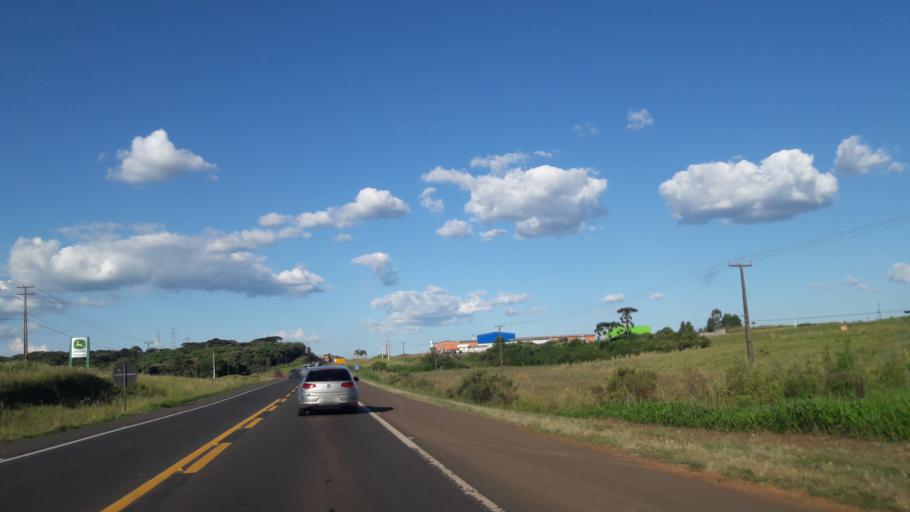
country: BR
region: Parana
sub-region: Guarapuava
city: Guarapuava
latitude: -25.3754
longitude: -51.5026
